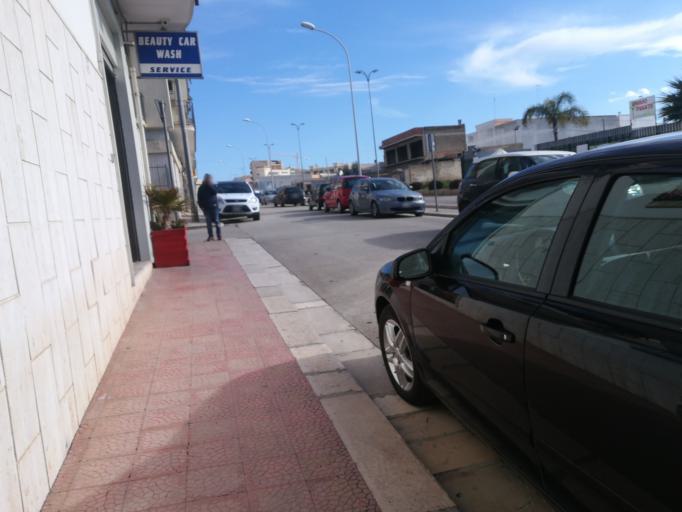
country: IT
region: Apulia
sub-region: Provincia di Barletta - Andria - Trani
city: Andria
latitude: 41.2182
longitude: 16.3007
